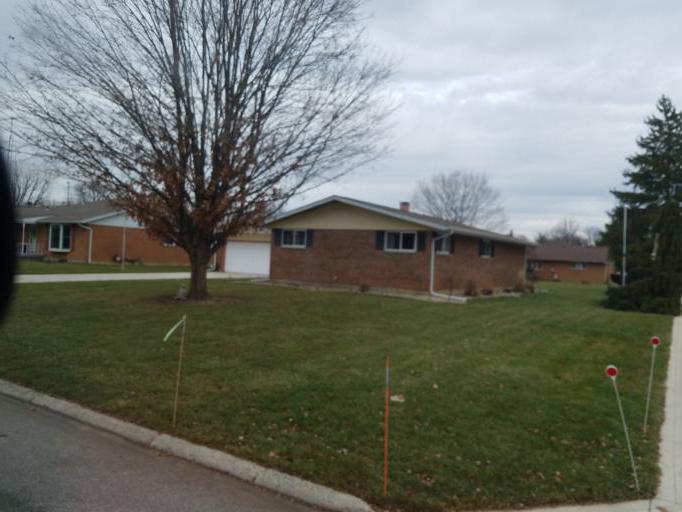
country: US
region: Ohio
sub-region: Marion County
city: Marion
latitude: 40.5744
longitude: -83.0815
